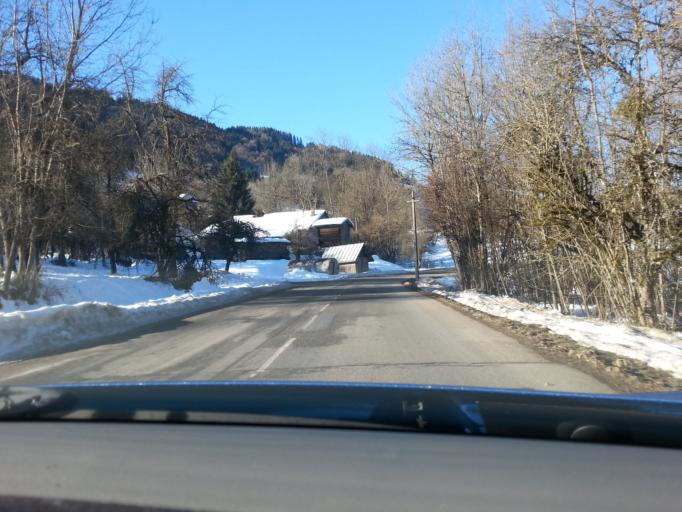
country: FR
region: Rhone-Alpes
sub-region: Departement de la Haute-Savoie
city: Samoens
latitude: 46.0748
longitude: 6.7072
